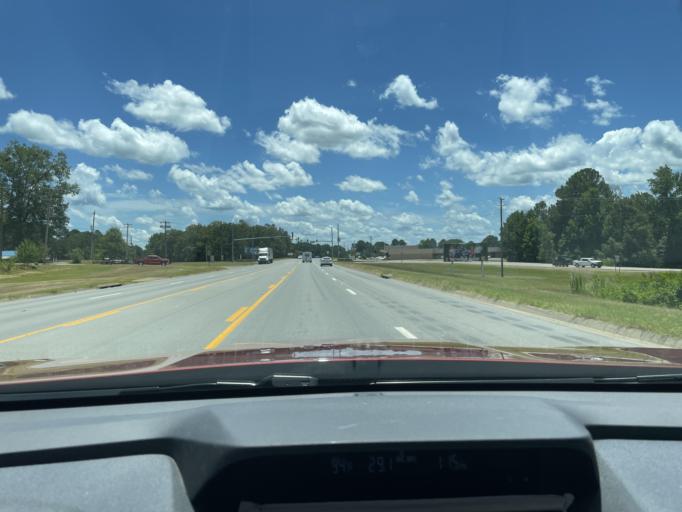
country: US
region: Arkansas
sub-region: Drew County
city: Monticello
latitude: 33.6498
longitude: -91.8019
